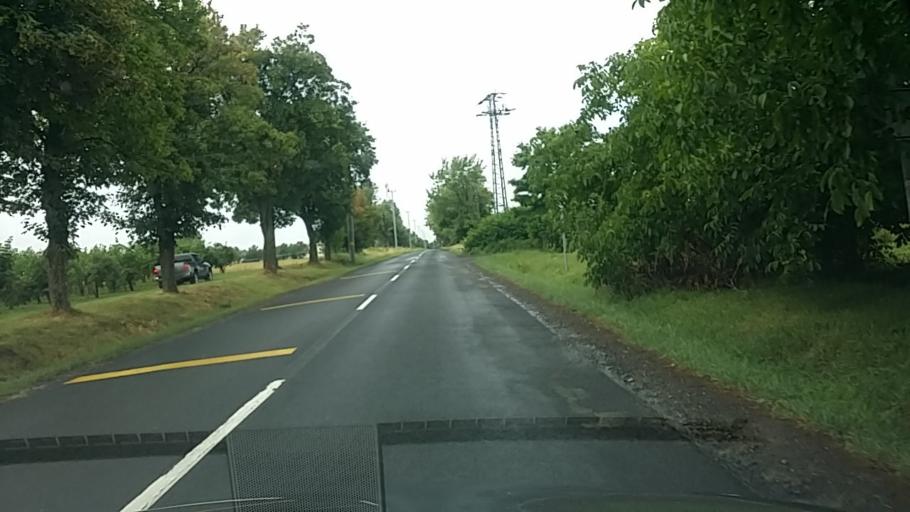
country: SK
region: Nitriansky
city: Sahy
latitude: 48.0142
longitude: 18.8849
